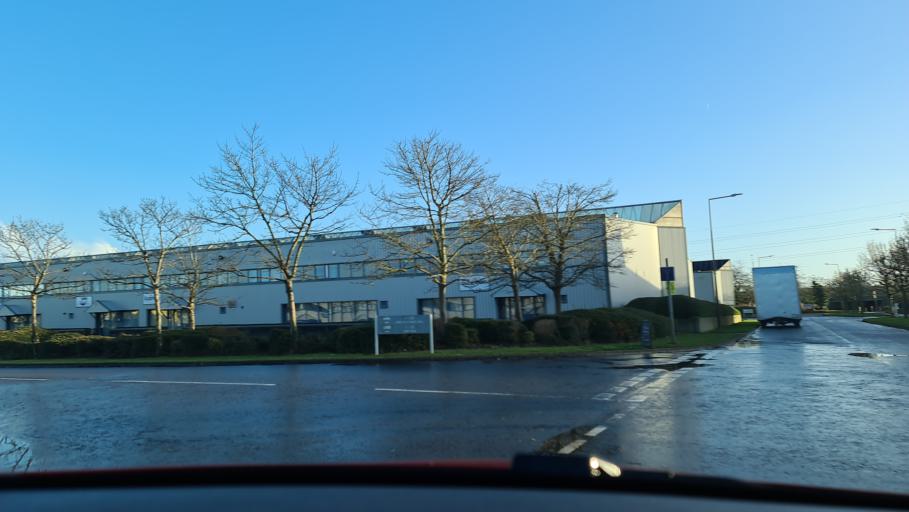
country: GB
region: England
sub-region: Milton Keynes
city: Bradwell
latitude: 52.0501
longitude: -0.8024
